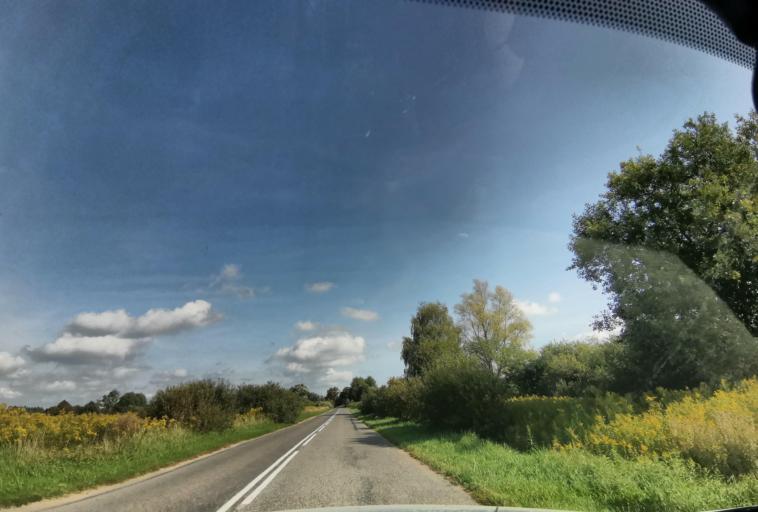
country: RU
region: Kaliningrad
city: Chernyakhovsk
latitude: 54.6531
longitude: 21.8830
